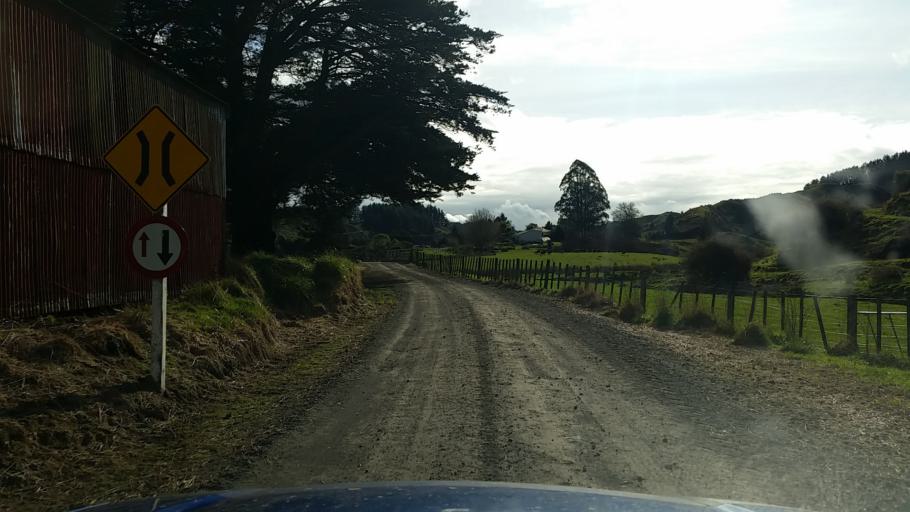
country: NZ
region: Taranaki
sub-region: South Taranaki District
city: Eltham
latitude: -39.2597
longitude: 174.5770
